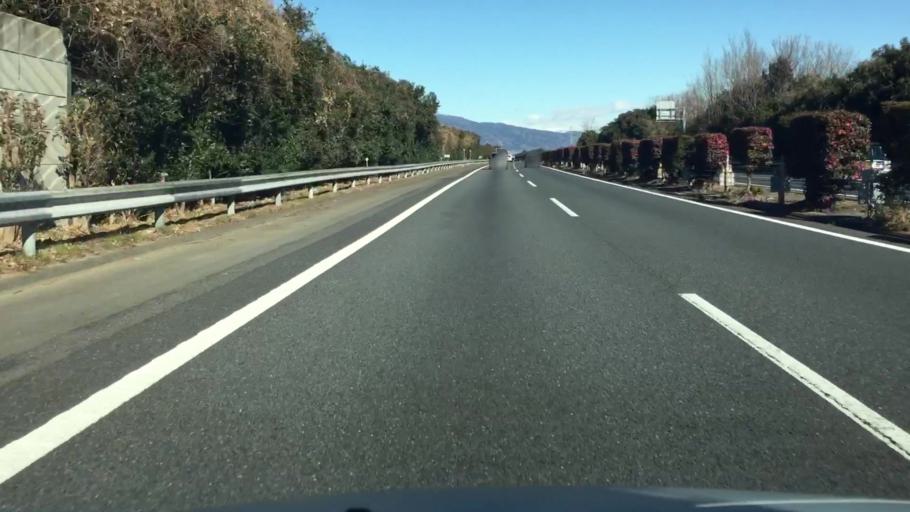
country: JP
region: Gunma
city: Kanekomachi
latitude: 36.4397
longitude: 139.0143
